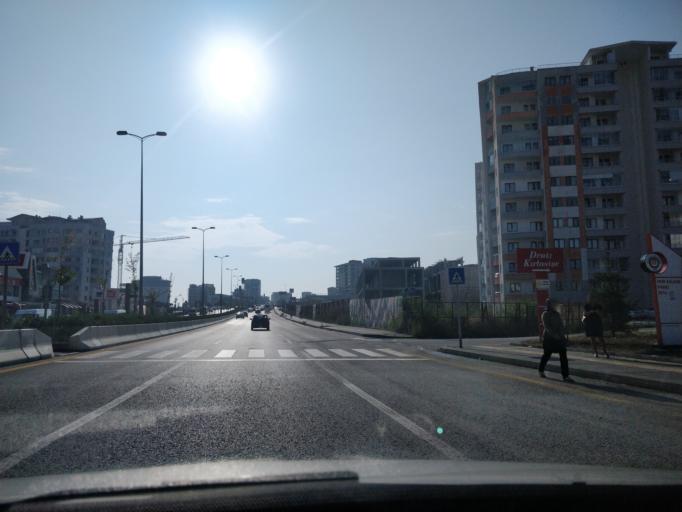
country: TR
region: Ankara
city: Etimesgut
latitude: 39.8978
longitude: 32.6428
